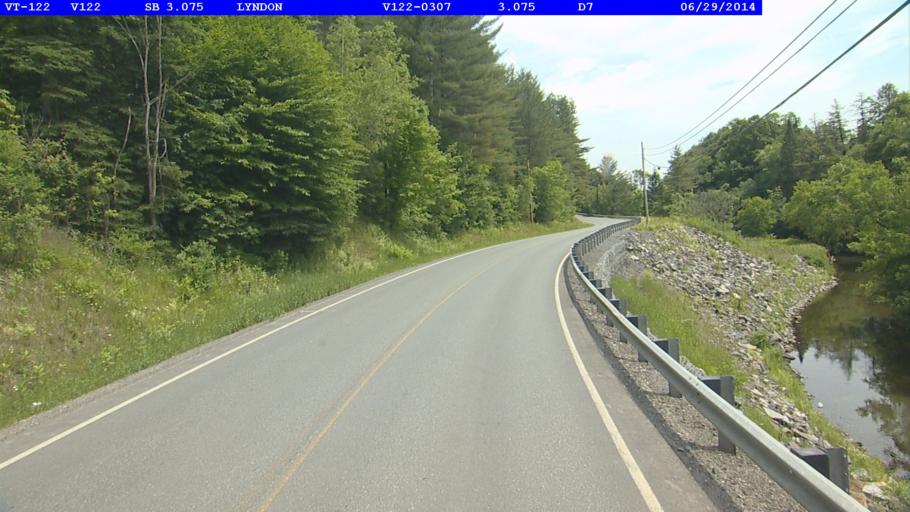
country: US
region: Vermont
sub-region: Caledonia County
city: Lyndonville
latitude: 44.5681
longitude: -72.0440
